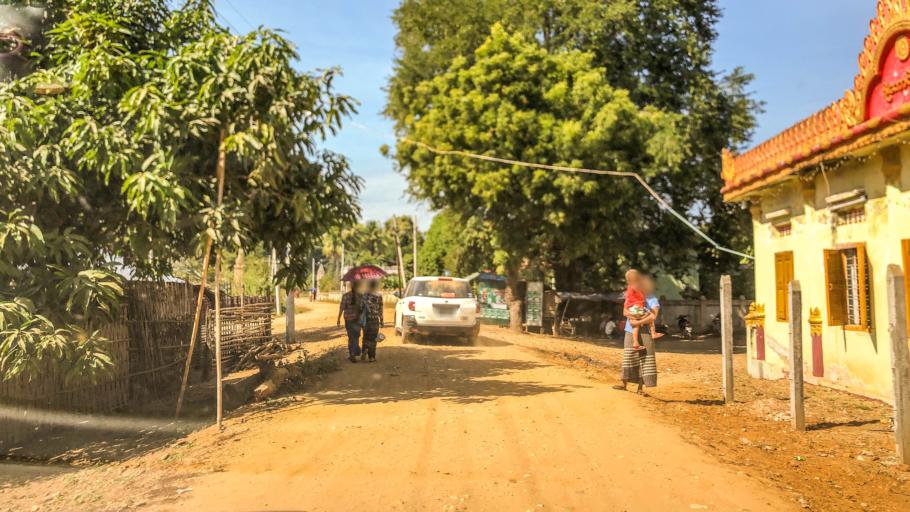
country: MM
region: Magway
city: Magway
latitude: 19.9753
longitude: 95.0369
